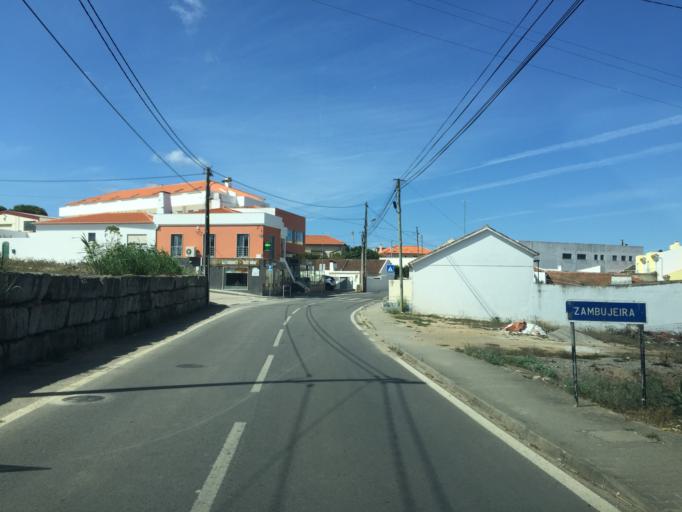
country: PT
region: Lisbon
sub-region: Lourinha
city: Lourinha
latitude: 39.2690
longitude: -9.3087
